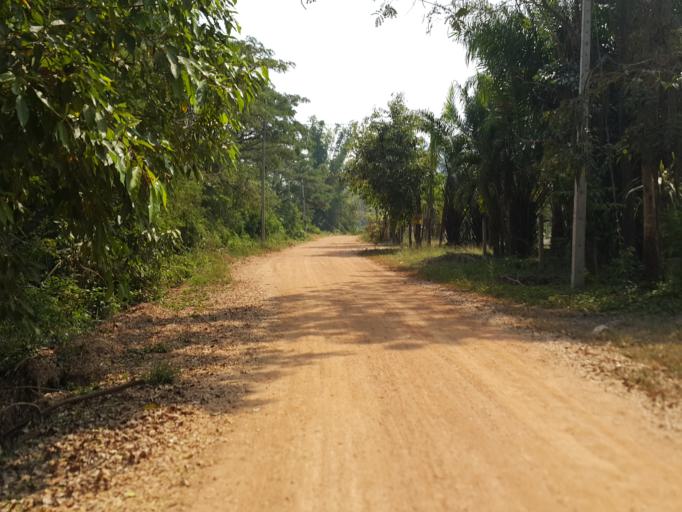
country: TH
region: Sukhothai
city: Thung Saliam
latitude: 17.3317
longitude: 99.4933
